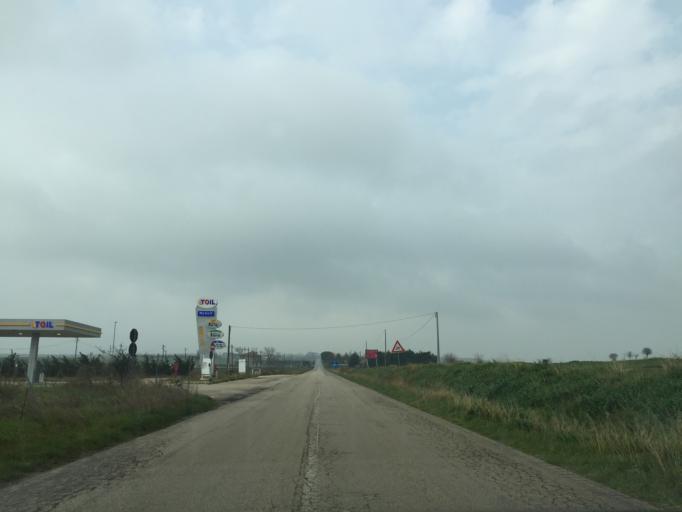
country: IT
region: Apulia
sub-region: Provincia di Foggia
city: Troia
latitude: 41.3791
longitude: 15.3676
